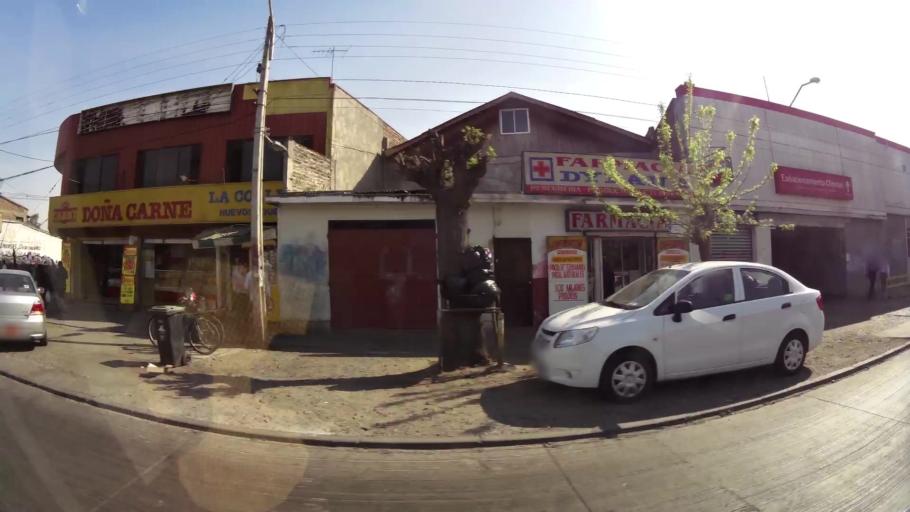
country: CL
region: Santiago Metropolitan
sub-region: Provincia de Santiago
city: Lo Prado
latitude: -33.4294
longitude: -70.7367
